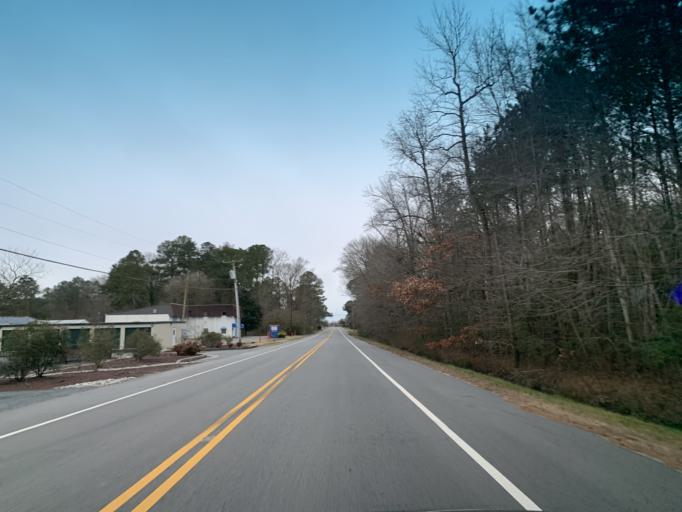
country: US
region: Maryland
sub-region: Worcester County
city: Pocomoke City
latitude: 38.0728
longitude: -75.5462
